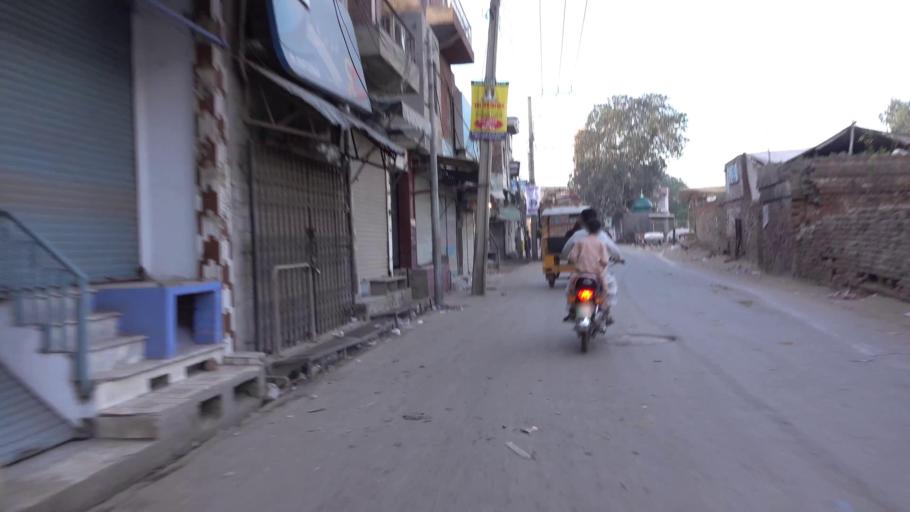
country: PK
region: Punjab
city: Hafizabad
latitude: 32.0703
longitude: 73.6893
